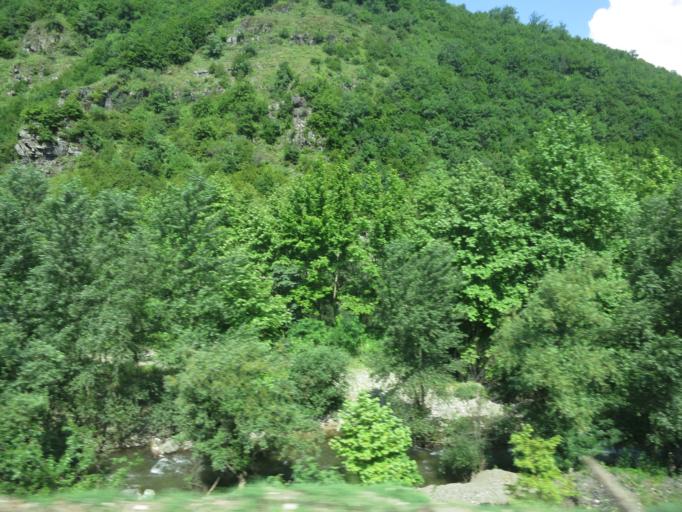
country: GE
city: Shorapani
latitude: 42.0844
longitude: 43.1417
